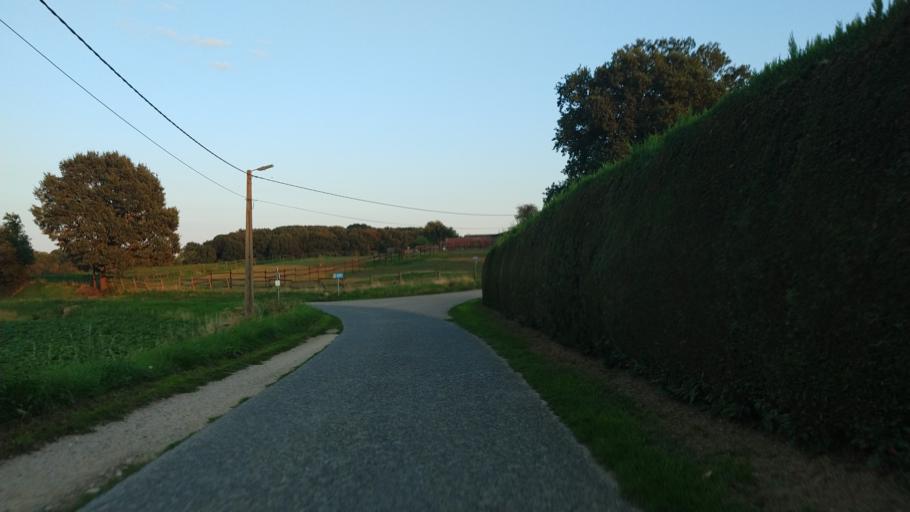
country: BE
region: Flanders
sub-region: Provincie Vlaams-Brabant
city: Lubbeek
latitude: 50.8753
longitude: 4.8223
